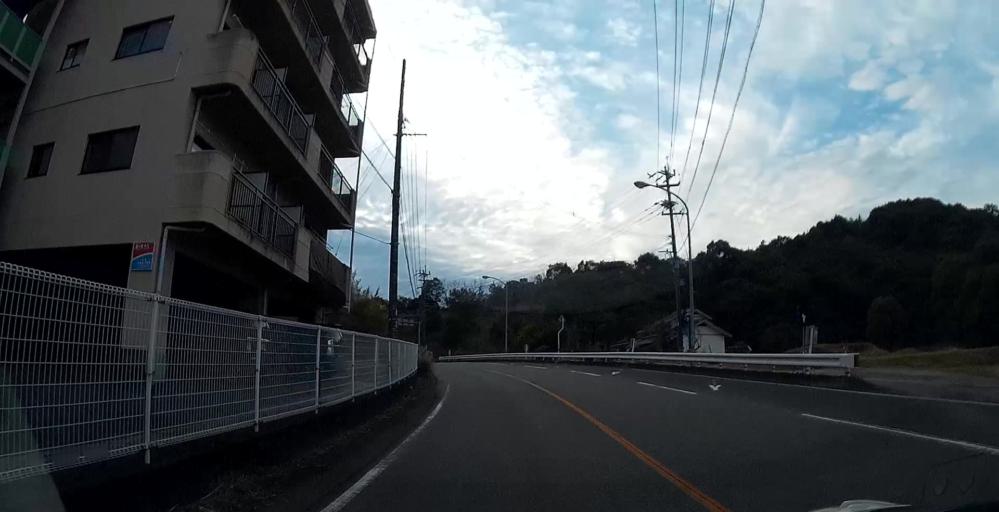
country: JP
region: Kumamoto
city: Yatsushiro
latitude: 32.4966
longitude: 130.4210
